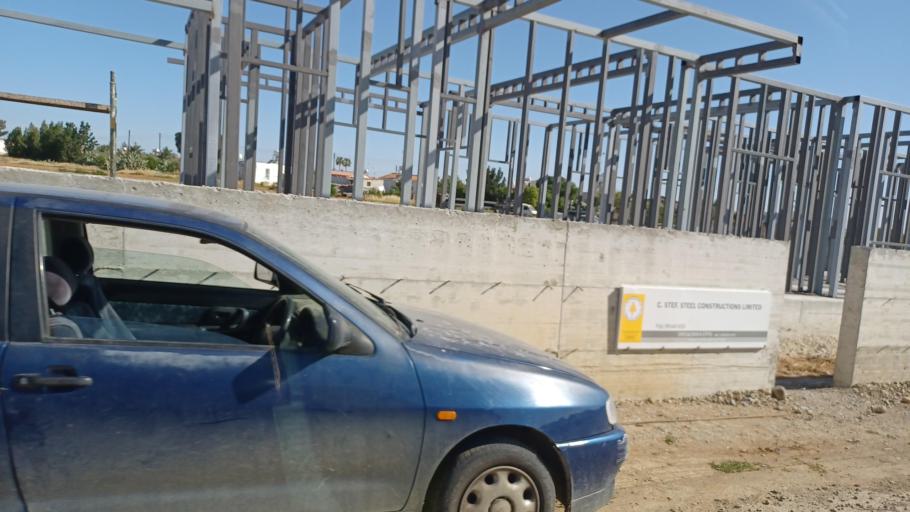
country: CY
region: Lefkosia
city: Kokkinotrimithia
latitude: 35.1525
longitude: 33.1878
